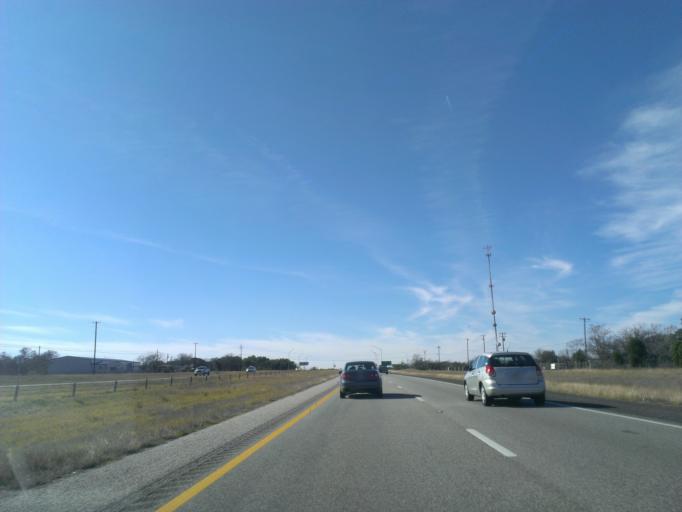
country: US
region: Texas
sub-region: Bell County
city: Belton
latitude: 31.0561
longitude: -97.5211
